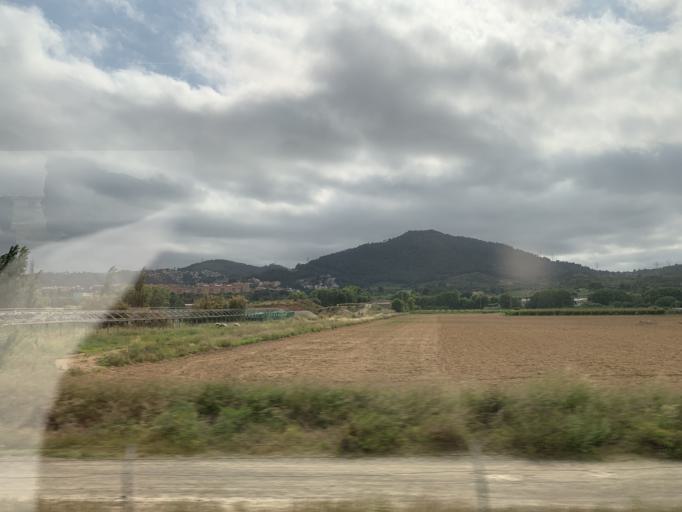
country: ES
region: Catalonia
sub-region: Provincia de Barcelona
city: Santa Coloma de Cervello
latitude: 41.3765
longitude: 2.0282
